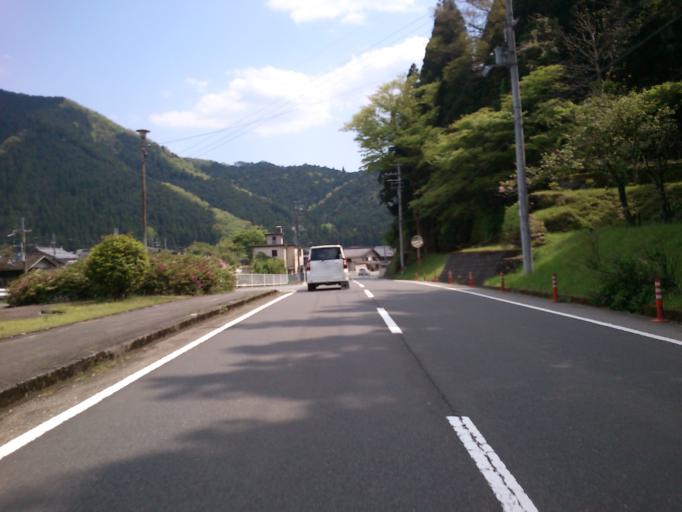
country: JP
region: Kyoto
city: Fukuchiyama
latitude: 35.3516
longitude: 134.9445
